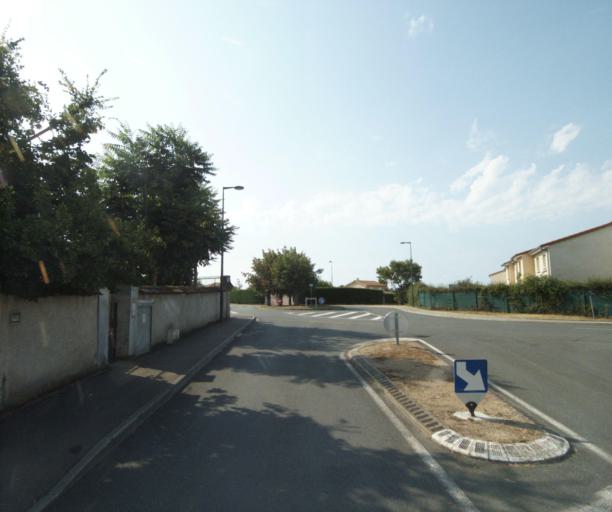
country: FR
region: Rhone-Alpes
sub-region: Departement du Rhone
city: Saint-Germain-Nuelles
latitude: 45.8332
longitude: 4.6082
